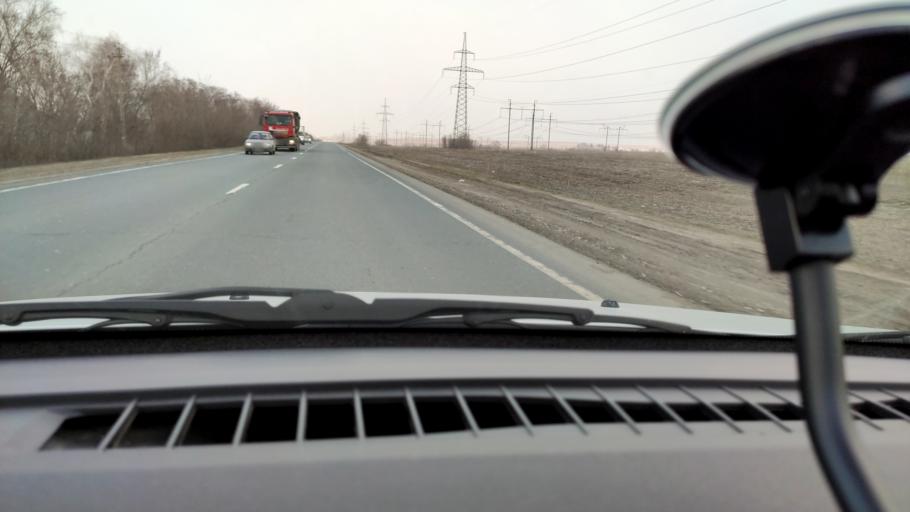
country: RU
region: Samara
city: Dubovyy Umet
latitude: 53.0746
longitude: 50.3853
